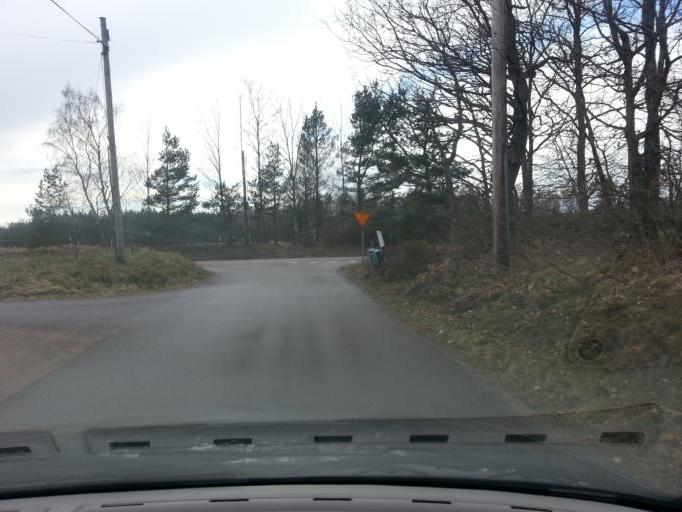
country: SE
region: Skane
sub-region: Klippans Kommun
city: Ljungbyhed
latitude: 56.0895
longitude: 13.2805
